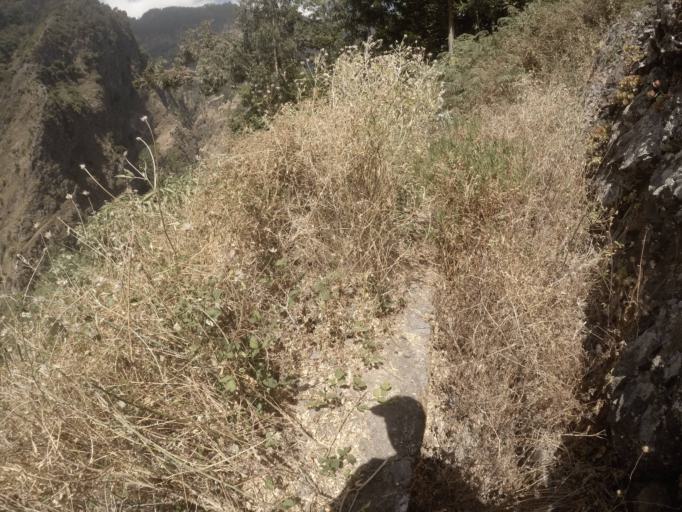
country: PT
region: Madeira
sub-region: Camara de Lobos
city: Curral das Freiras
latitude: 32.7026
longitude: -16.9644
